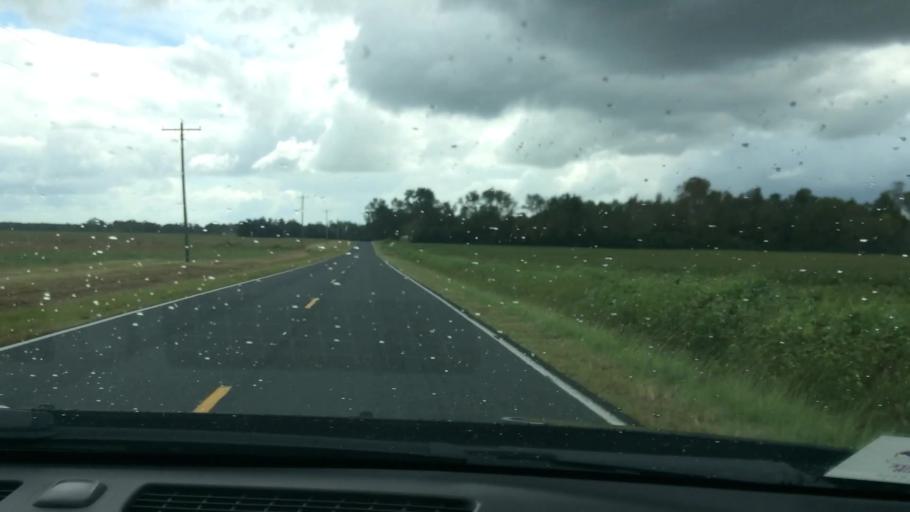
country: US
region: North Carolina
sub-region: Greene County
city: Maury
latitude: 35.5077
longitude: -77.5253
